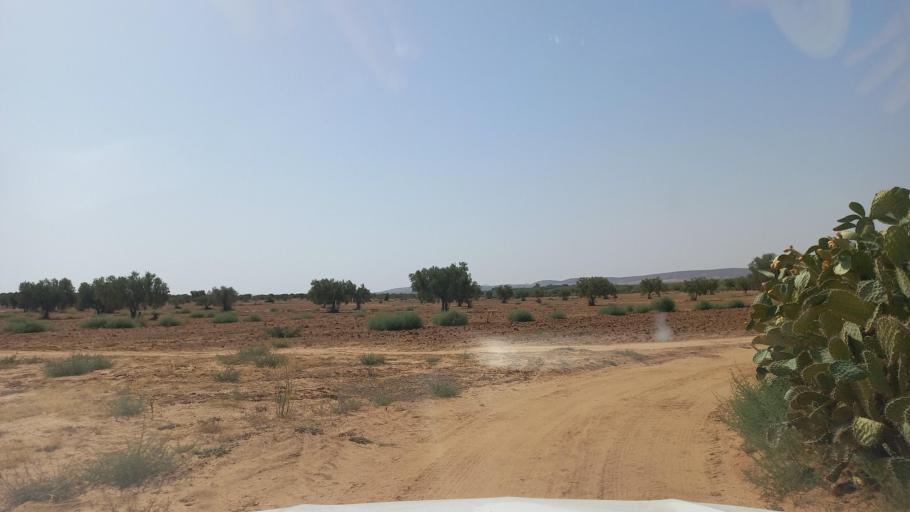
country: TN
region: Al Qasrayn
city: Kasserine
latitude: 35.2441
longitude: 9.0598
